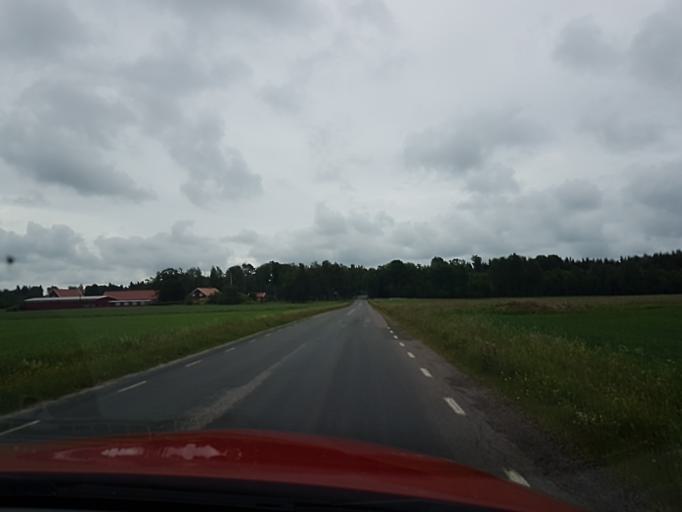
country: SE
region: Vaestra Goetaland
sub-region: Tidaholms Kommun
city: Olofstorp
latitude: 58.3314
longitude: 13.9894
